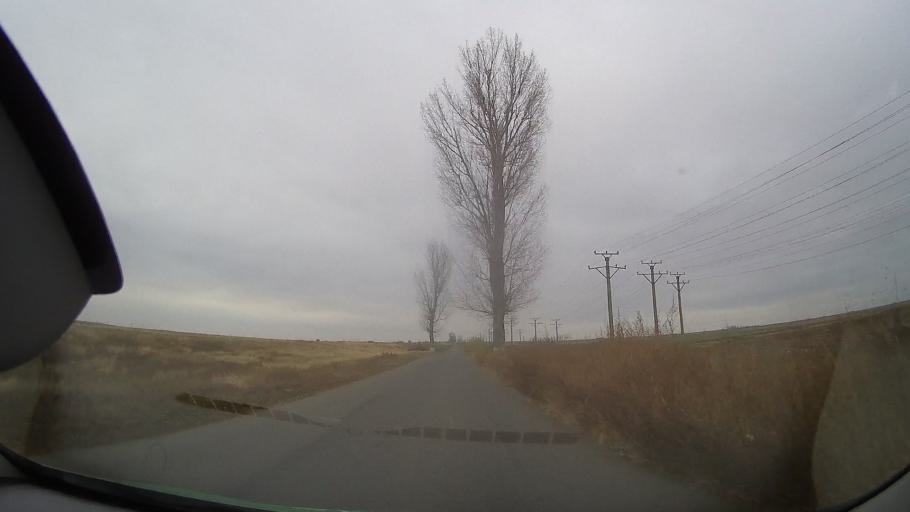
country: RO
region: Braila
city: Dudesti
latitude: 44.9073
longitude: 27.4313
